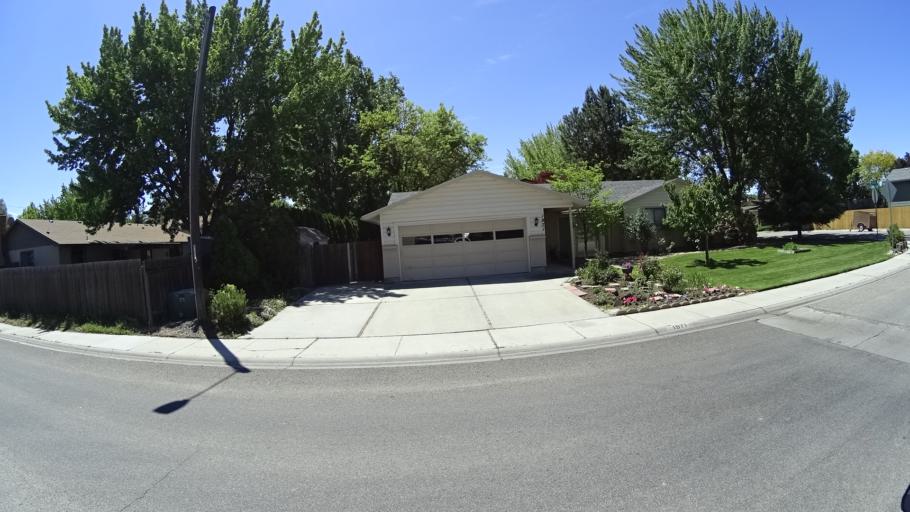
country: US
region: Idaho
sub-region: Ada County
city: Boise
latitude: 43.5678
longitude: -116.1601
